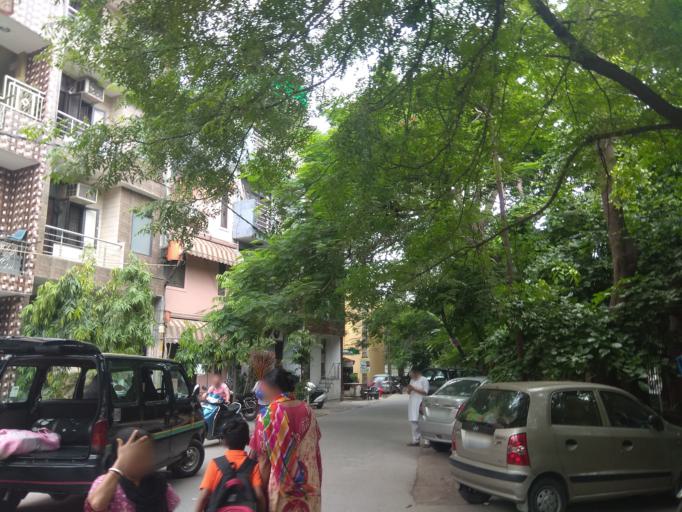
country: IN
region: NCT
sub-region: New Delhi
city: New Delhi
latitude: 28.5715
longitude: 77.2460
